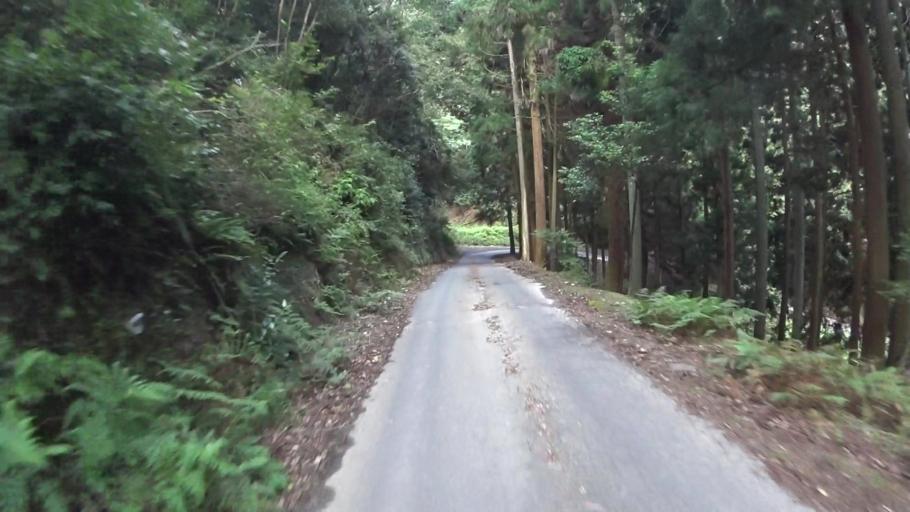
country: JP
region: Shiga Prefecture
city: Otsu-shi
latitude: 34.9465
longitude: 135.8444
